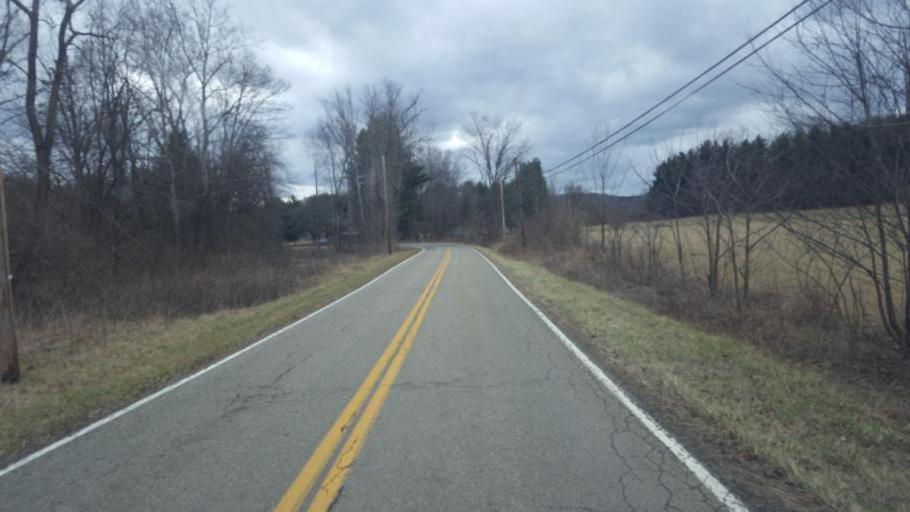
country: US
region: Ohio
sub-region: Licking County
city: Newark
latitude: 40.1691
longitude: -82.2968
